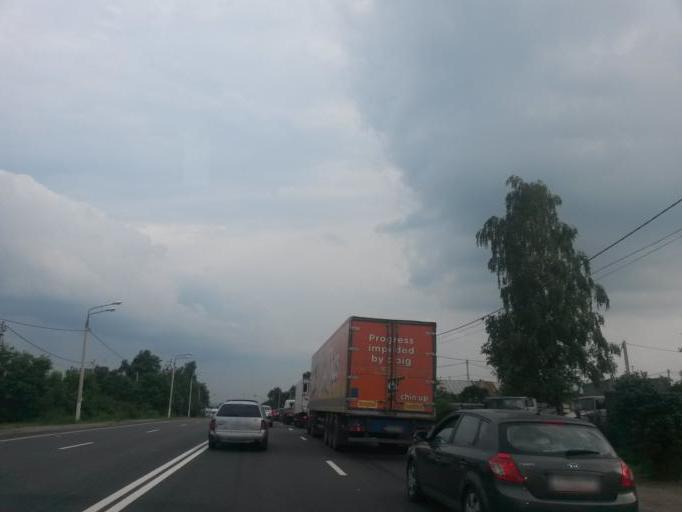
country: RU
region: Moskovskaya
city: Gorki-Leninskiye
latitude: 55.5102
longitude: 37.7556
